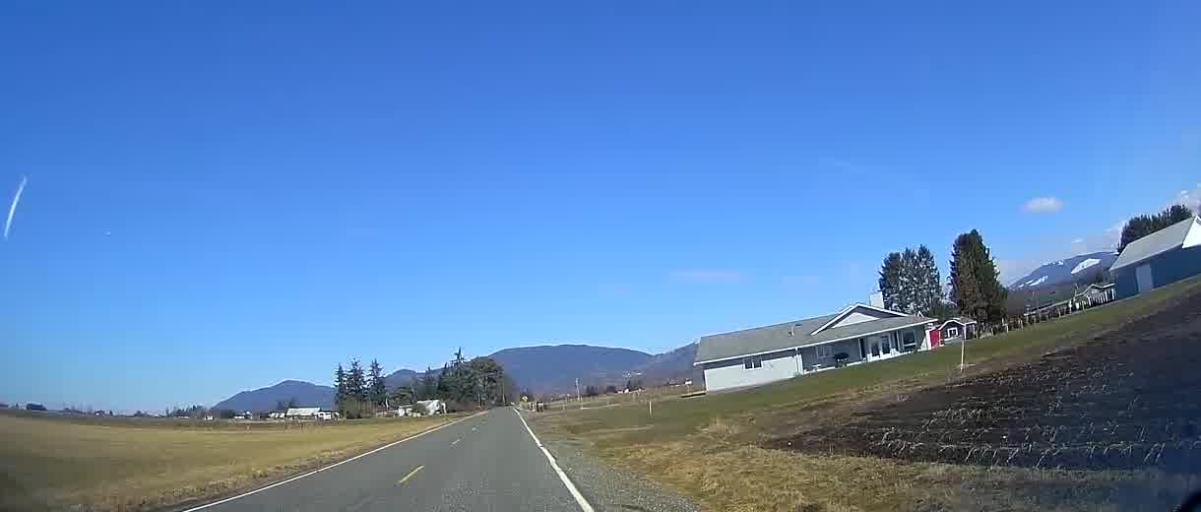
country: US
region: Washington
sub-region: Skagit County
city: Burlington
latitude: 48.5482
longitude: -122.4113
